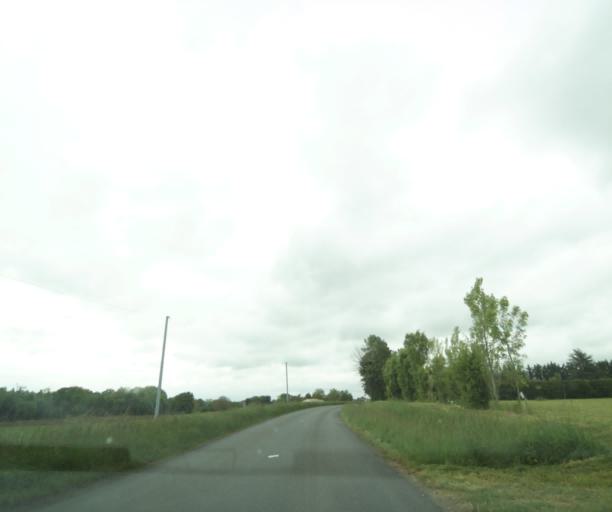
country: FR
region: Poitou-Charentes
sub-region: Departement de la Charente-Maritime
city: Chaniers
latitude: 45.7029
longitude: -0.5528
